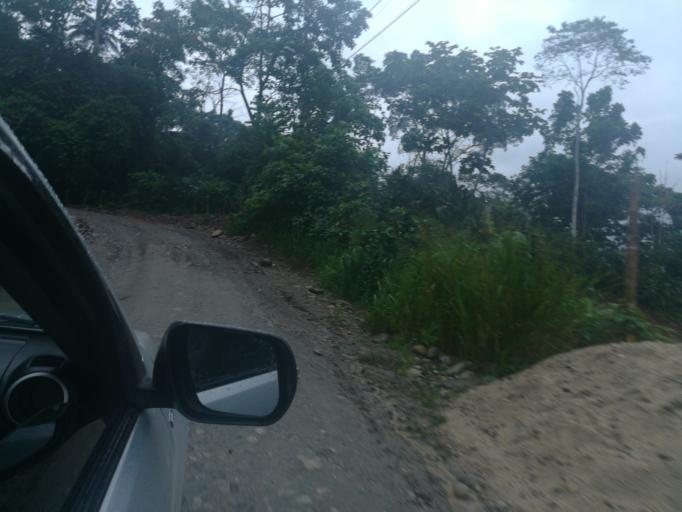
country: EC
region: Napo
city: Tena
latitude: -1.0376
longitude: -77.6630
